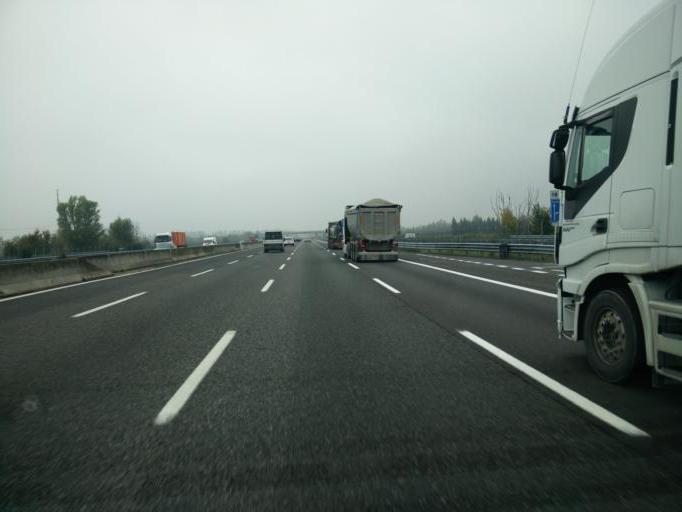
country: IT
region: Emilia-Romagna
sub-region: Provincia di Modena
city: Baggiovara
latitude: 44.6229
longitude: 10.8821
